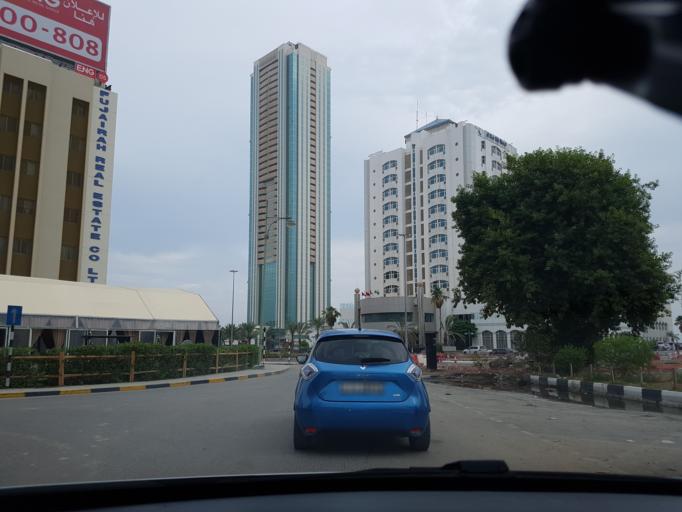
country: AE
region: Al Fujayrah
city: Al Fujayrah
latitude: 25.1227
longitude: 56.3319
